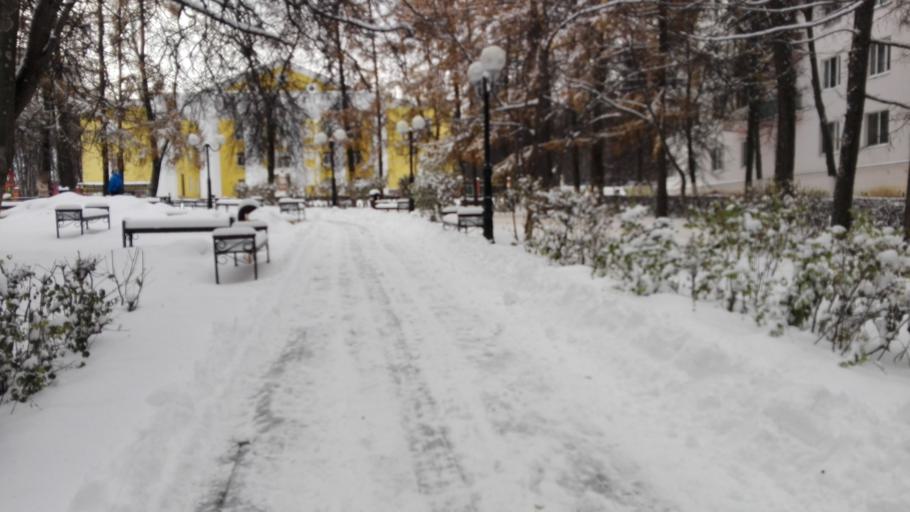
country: RU
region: Tula
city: Kosaya Gora
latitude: 54.1208
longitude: 37.5454
